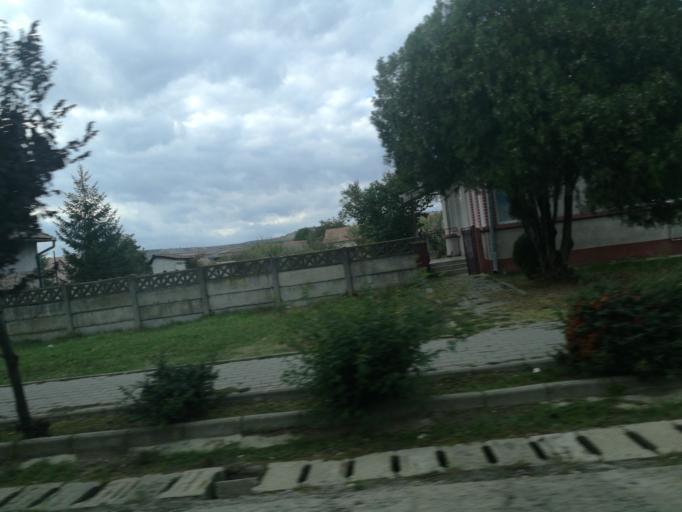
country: RO
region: Mures
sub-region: Comuna Ungheni
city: Ungheni
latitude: 46.4851
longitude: 24.4590
